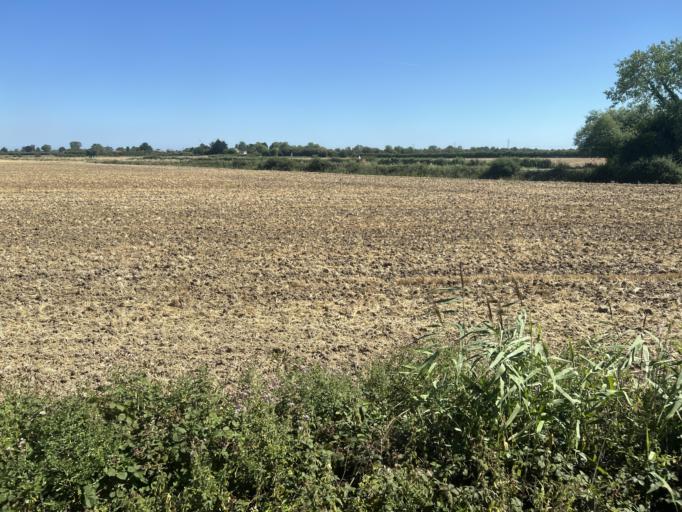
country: GB
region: England
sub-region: Lincolnshire
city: Wainfleet All Saints
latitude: 53.1242
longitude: 0.1983
